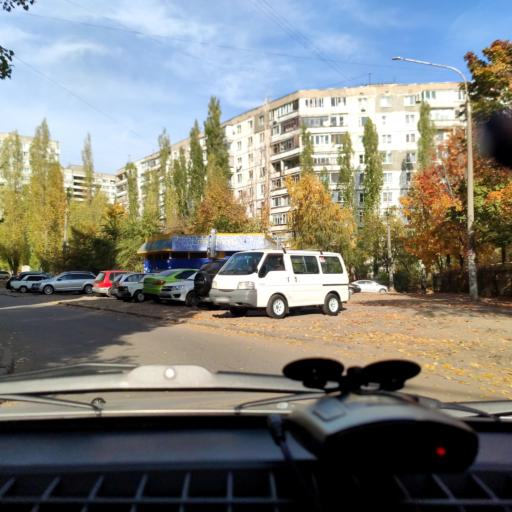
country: RU
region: Voronezj
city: Podgornoye
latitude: 51.7026
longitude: 39.1547
